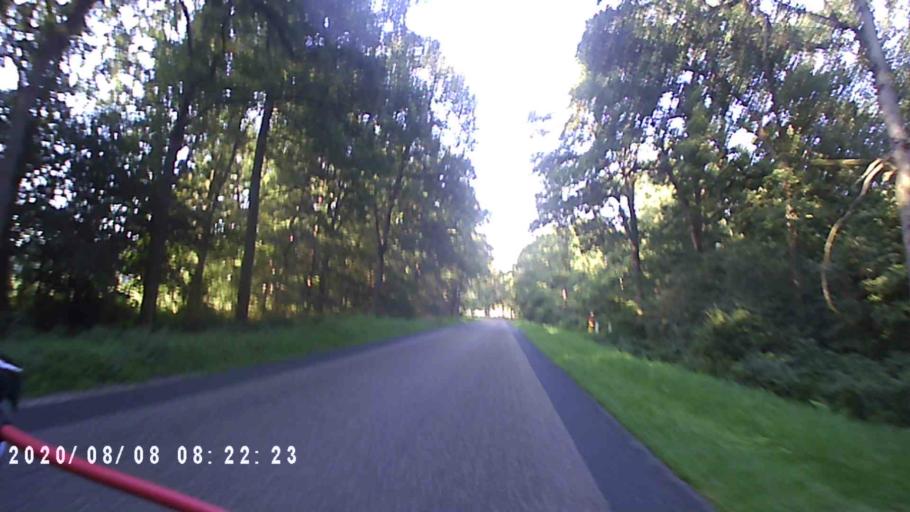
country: NL
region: Groningen
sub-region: Gemeente Leek
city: Leek
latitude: 53.0904
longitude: 6.3122
